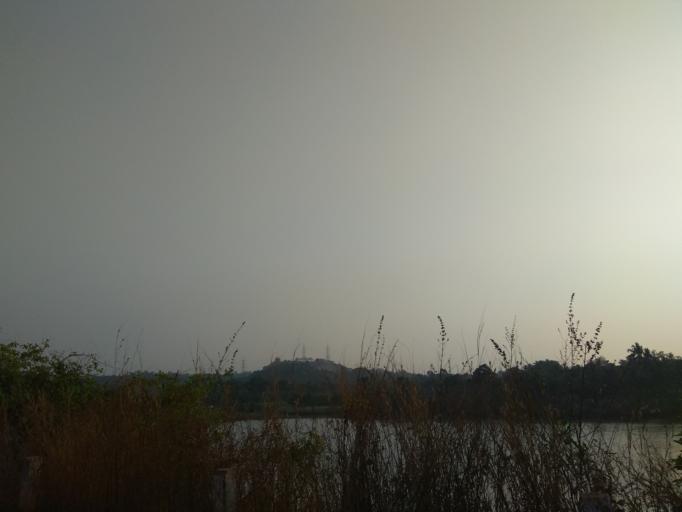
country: IN
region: Karnataka
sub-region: Dakshina Kannada
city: Mangalore
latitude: 12.9401
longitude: 74.8685
